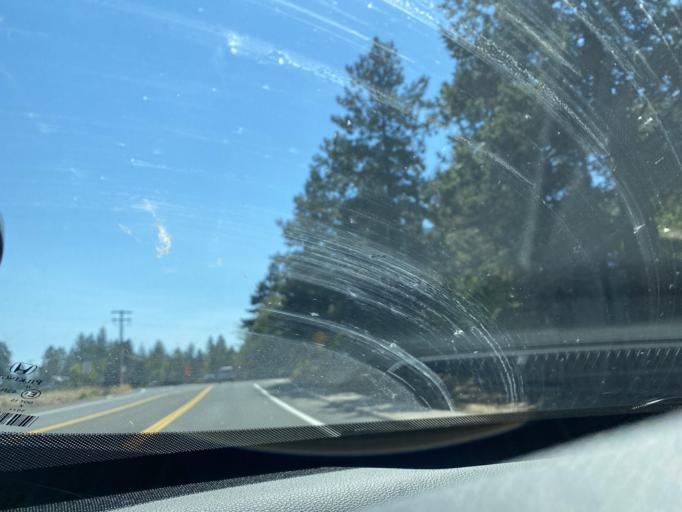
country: US
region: Oregon
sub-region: Deschutes County
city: Bend
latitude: 44.0629
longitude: -121.3399
